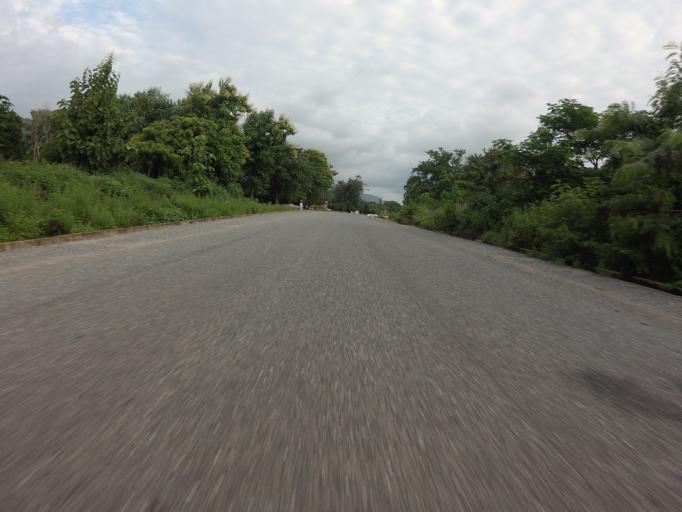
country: GH
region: Volta
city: Kpandu
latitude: 6.8503
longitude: 0.3932
